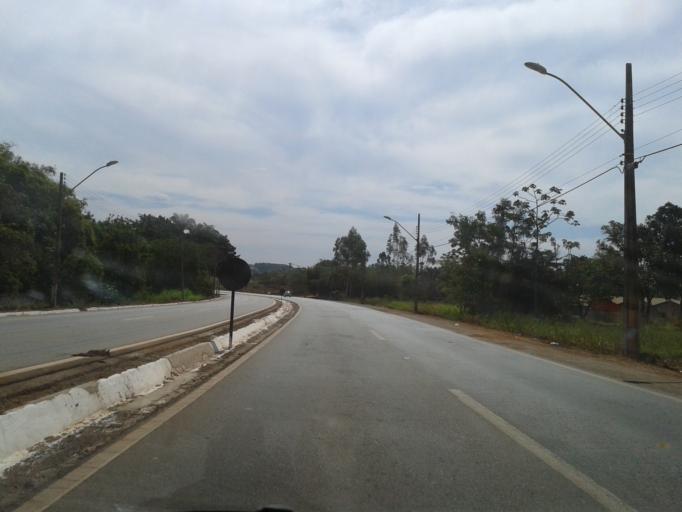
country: BR
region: Goias
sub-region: Goianira
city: Goianira
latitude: -16.4985
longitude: -49.4211
